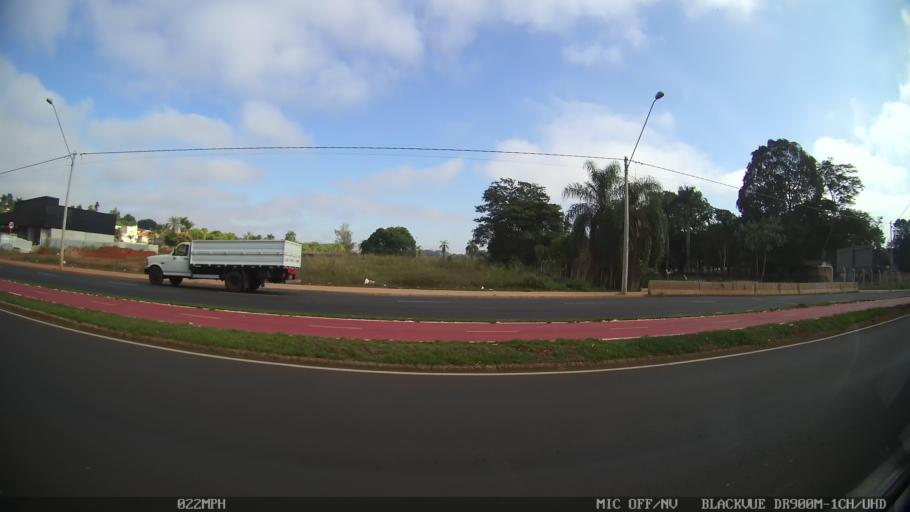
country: BR
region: Sao Paulo
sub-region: Sao Jose Do Rio Preto
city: Sao Jose do Rio Preto
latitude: -20.8123
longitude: -49.4335
